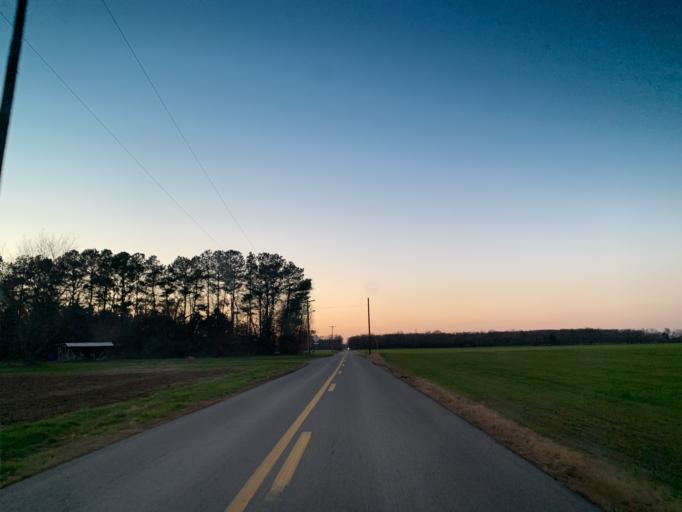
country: US
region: Delaware
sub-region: New Castle County
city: Middletown
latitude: 39.4106
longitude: -75.7500
